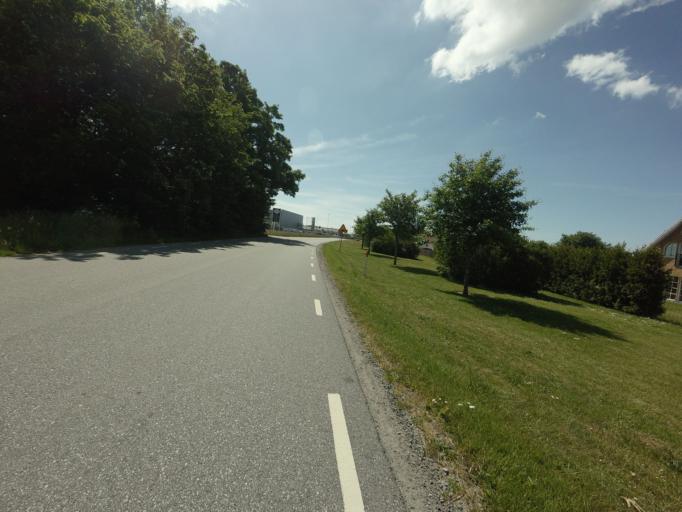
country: SE
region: Skane
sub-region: Trelleborgs Kommun
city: Skare
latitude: 55.4077
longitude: 13.0846
